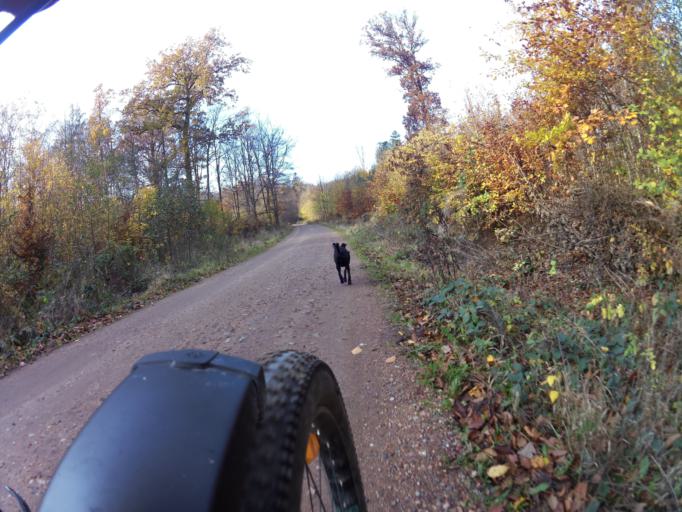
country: PL
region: Pomeranian Voivodeship
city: Strzelno
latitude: 54.7406
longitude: 18.2558
